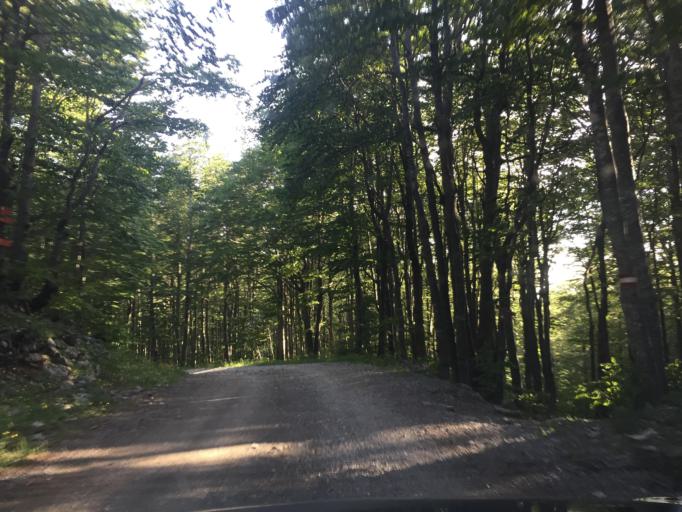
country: HR
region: Primorsko-Goranska
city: Podhum
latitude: 45.4323
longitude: 14.5761
